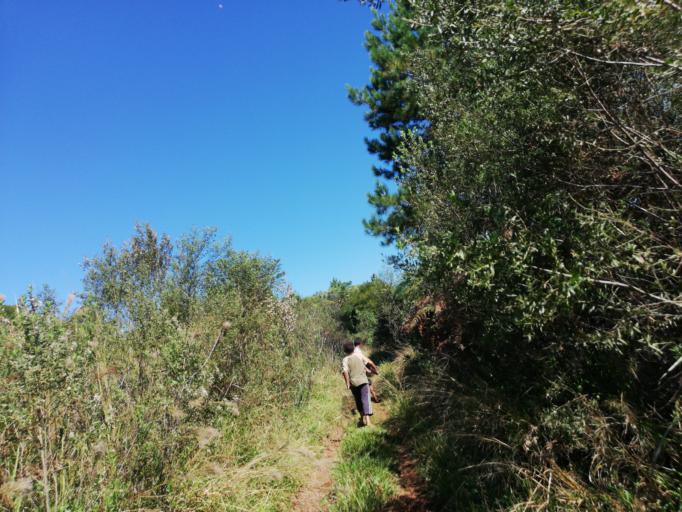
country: AR
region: Misiones
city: El Soberbio
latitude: -27.0625
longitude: -54.3769
